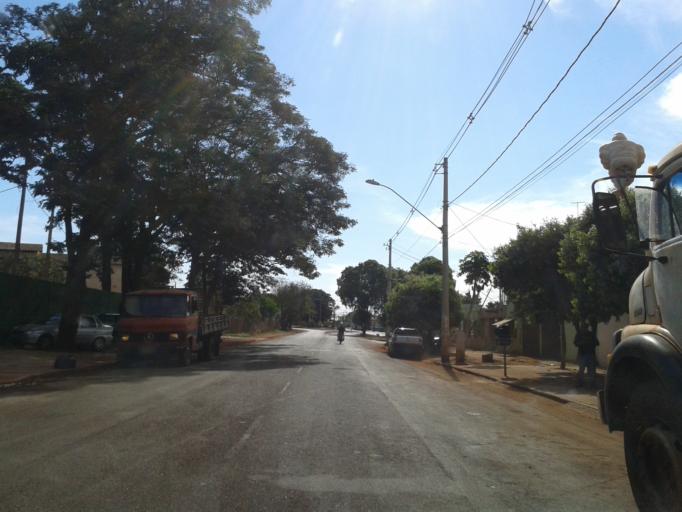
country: BR
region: Minas Gerais
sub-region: Ituiutaba
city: Ituiutaba
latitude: -18.9600
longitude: -49.4561
